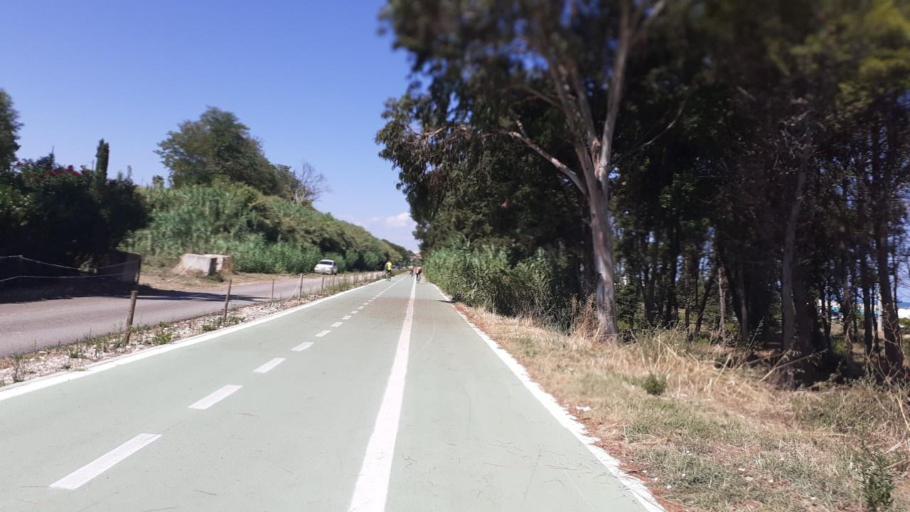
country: IT
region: Abruzzo
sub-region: Provincia di Chieti
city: Casalbordino-Miracoli
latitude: 42.2047
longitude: 14.6035
